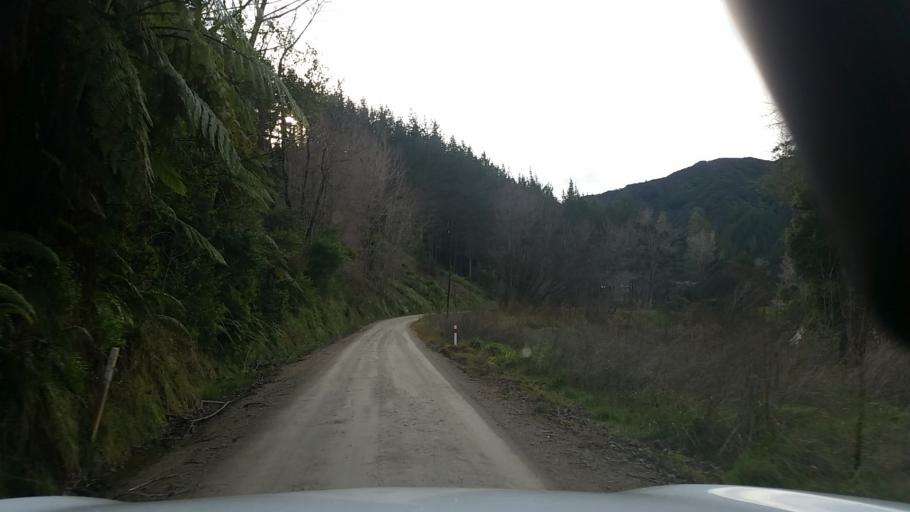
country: NZ
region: Taranaki
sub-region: South Taranaki District
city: Patea
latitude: -39.5783
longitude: 174.8254
